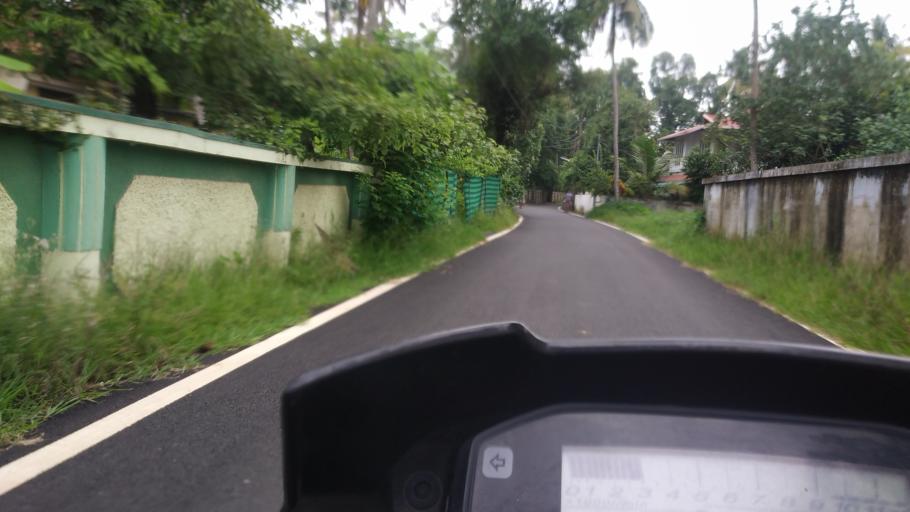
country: IN
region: Kerala
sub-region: Ernakulam
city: Elur
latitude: 10.0576
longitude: 76.2263
